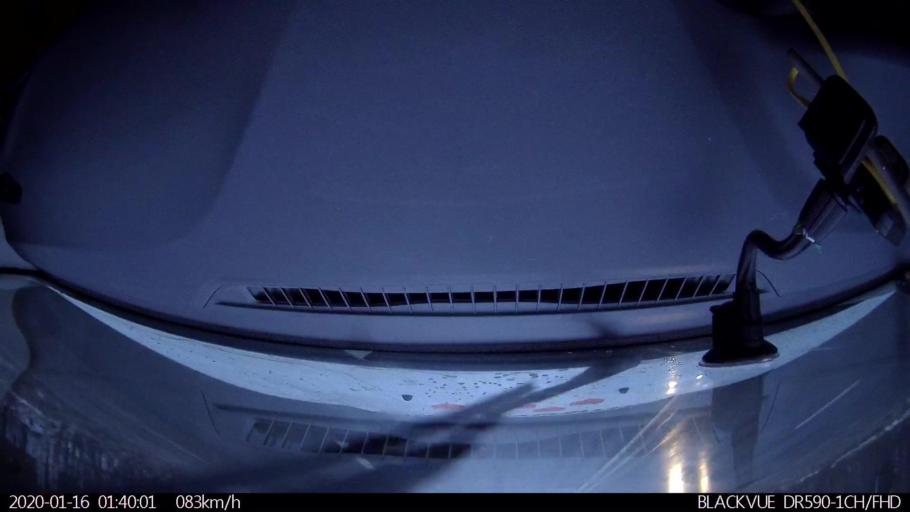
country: RU
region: Nizjnij Novgorod
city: Gorbatovka
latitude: 56.3298
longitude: 43.7852
